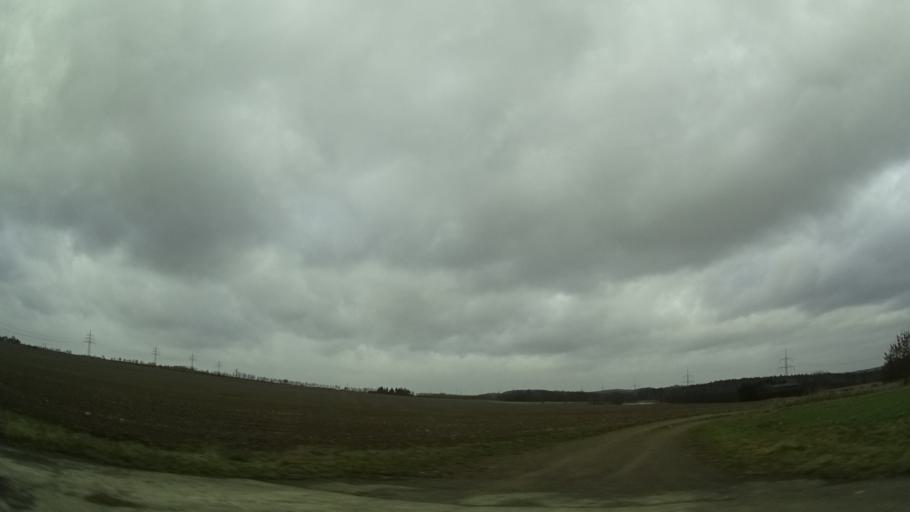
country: DE
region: Thuringia
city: Auma
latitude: 50.6840
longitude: 11.9155
